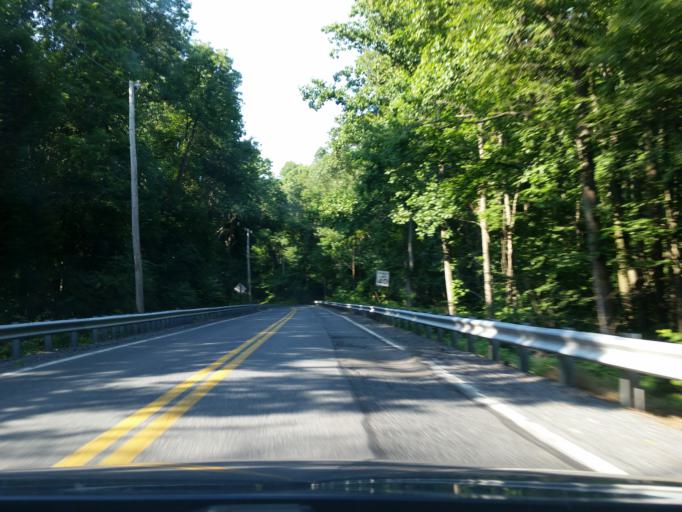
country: US
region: Pennsylvania
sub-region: Lebanon County
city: Campbelltown
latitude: 40.2275
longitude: -76.5048
